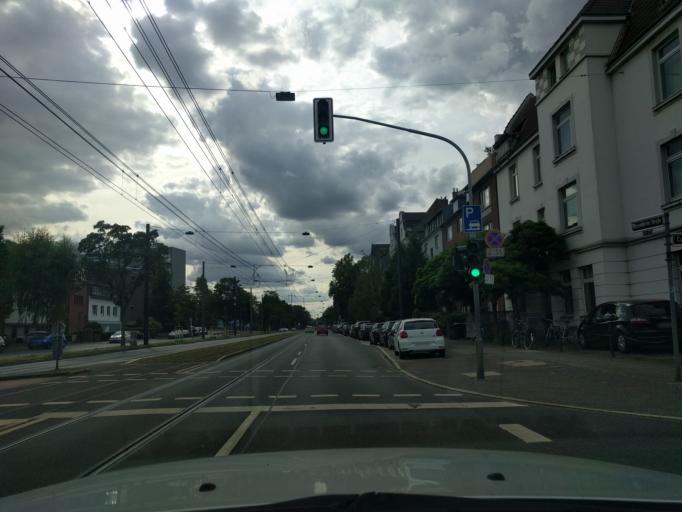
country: DE
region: North Rhine-Westphalia
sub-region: Regierungsbezirk Dusseldorf
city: Dusseldorf
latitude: 51.2303
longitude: 6.7421
